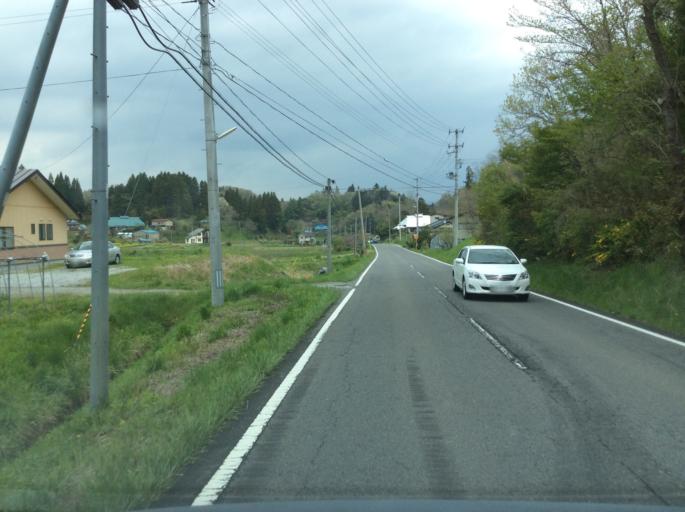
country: JP
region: Fukushima
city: Funehikimachi-funehiki
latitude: 37.3784
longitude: 140.5955
